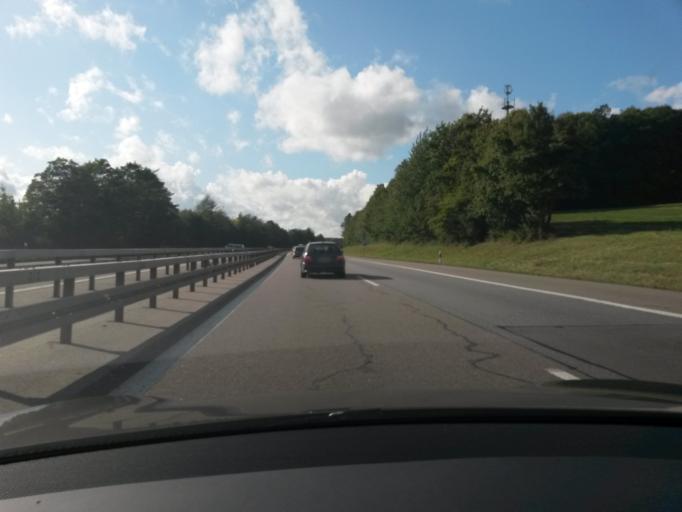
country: DE
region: Bavaria
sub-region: Upper Palatinate
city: Brunn
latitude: 49.0855
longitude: 11.8964
